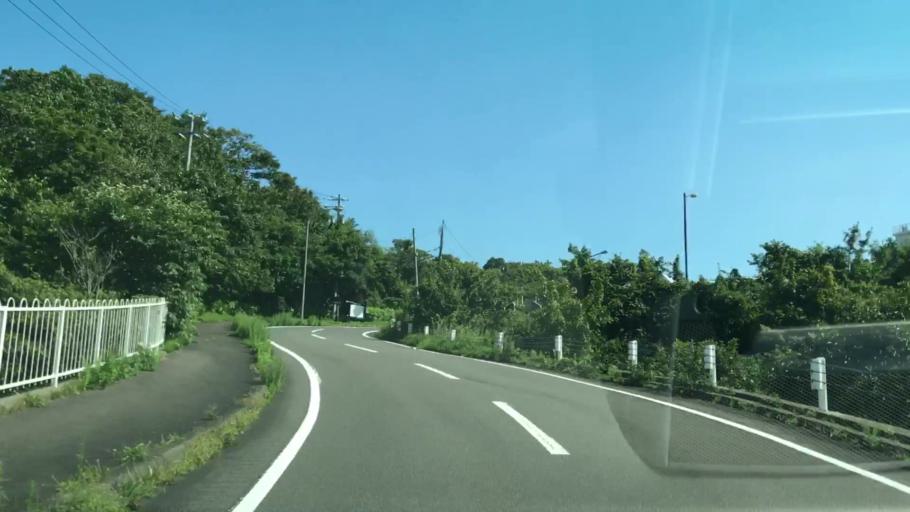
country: JP
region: Hokkaido
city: Muroran
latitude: 42.3041
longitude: 141.0004
